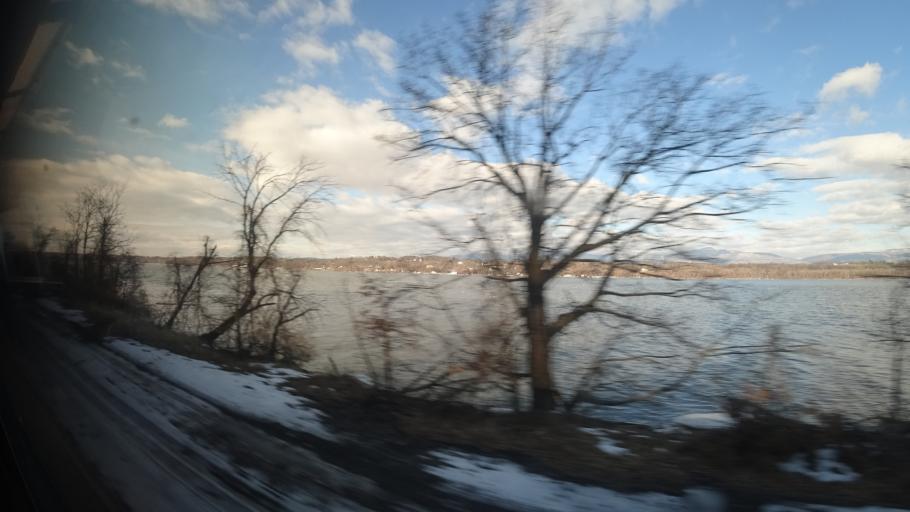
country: US
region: New York
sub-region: Dutchess County
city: Tivoli
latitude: 42.0964
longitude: -73.9175
